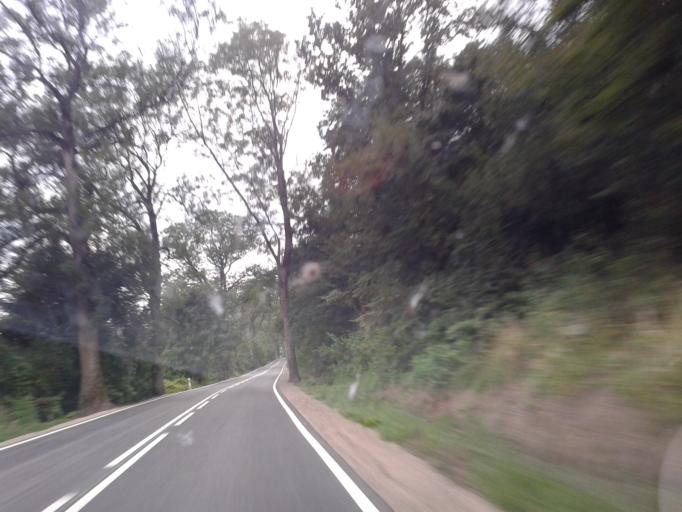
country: PL
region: West Pomeranian Voivodeship
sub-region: Powiat szczecinecki
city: Grzmiaca
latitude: 53.8542
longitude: 16.4694
